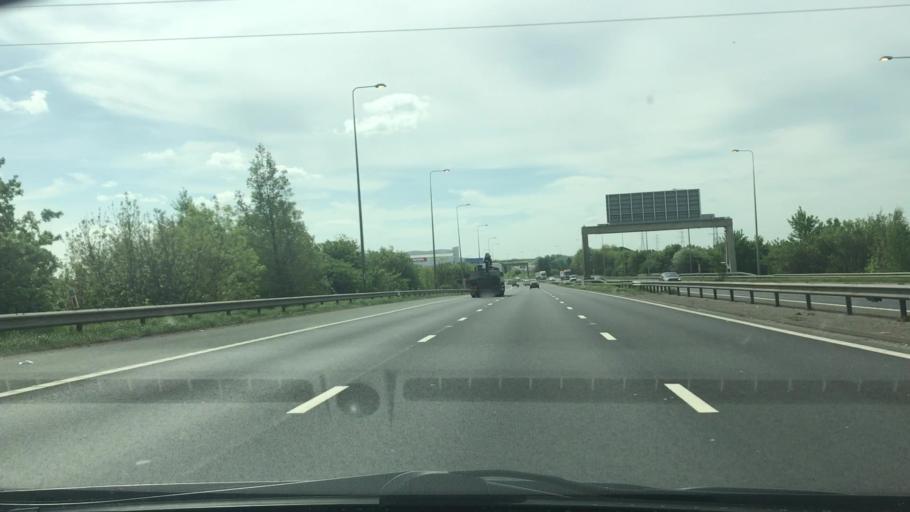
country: GB
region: England
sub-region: City and Borough of Wakefield
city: Ferrybridge
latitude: 53.7039
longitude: -1.2787
